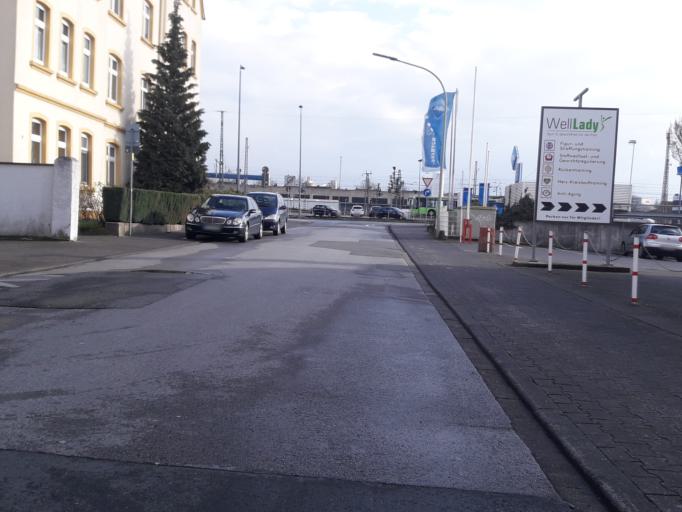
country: DE
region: North Rhine-Westphalia
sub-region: Regierungsbezirk Detmold
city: Paderborn
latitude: 51.7133
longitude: 8.7367
